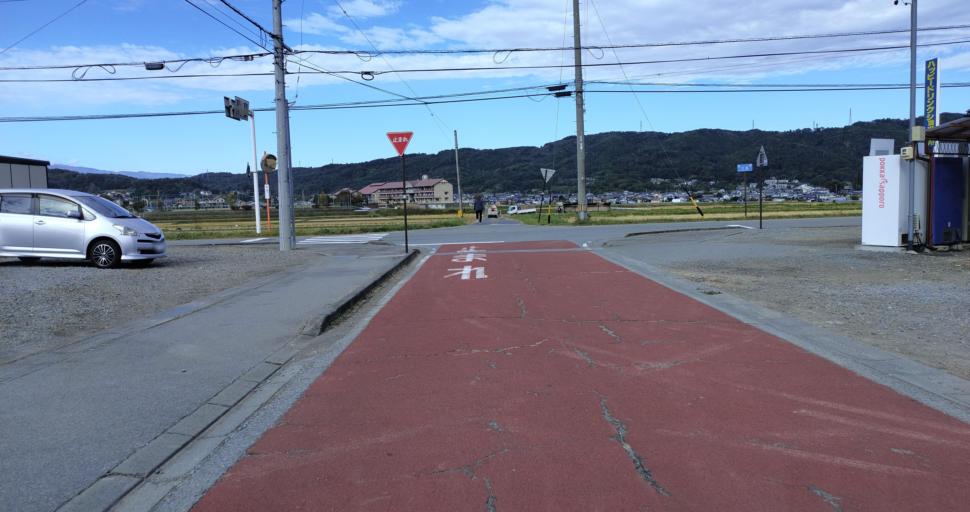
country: JP
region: Nagano
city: Komoro
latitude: 36.2693
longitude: 138.4054
